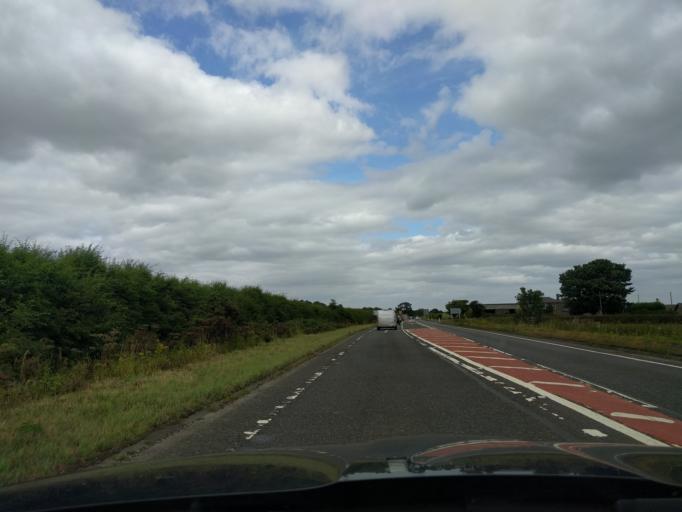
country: GB
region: England
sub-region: Northumberland
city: Ellingham
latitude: 55.4778
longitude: -1.7208
